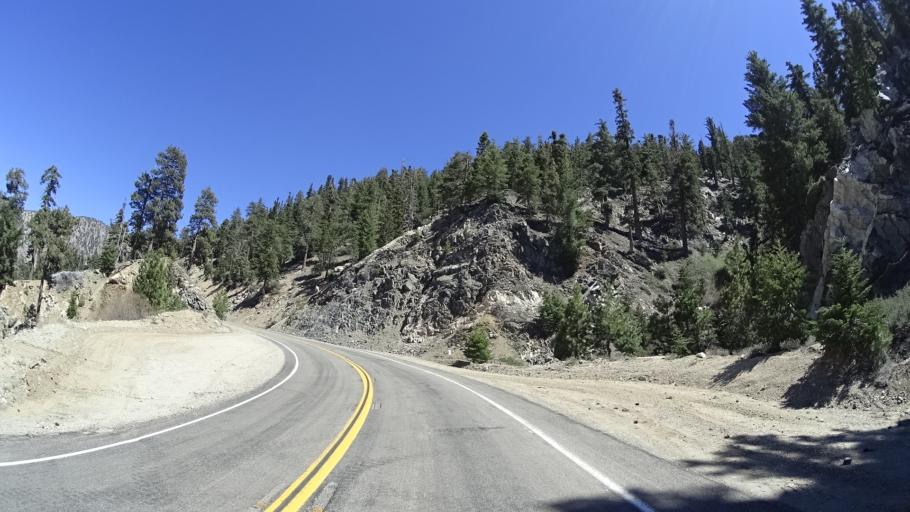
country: US
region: California
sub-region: San Bernardino County
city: Wrightwood
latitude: 34.3501
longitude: -117.8349
